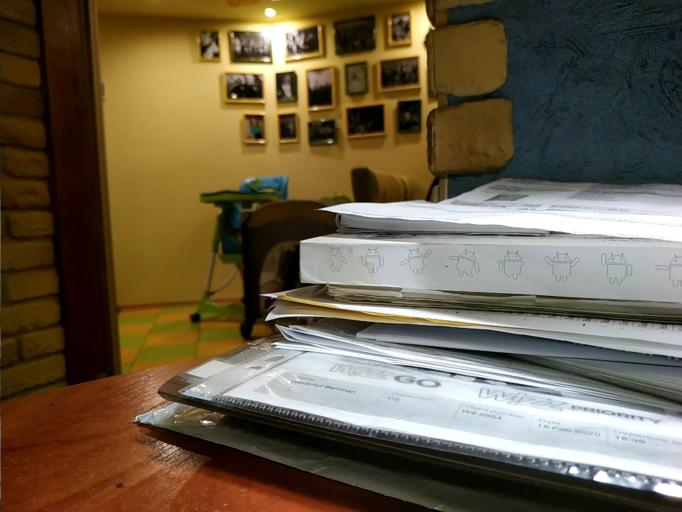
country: RU
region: Arkhangelskaya
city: Voloshka
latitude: 61.2100
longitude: 39.4940
